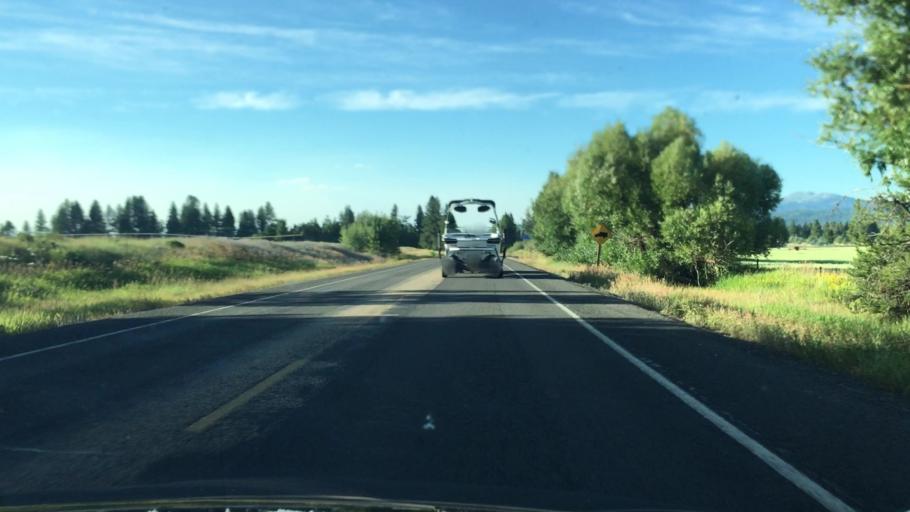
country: US
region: Idaho
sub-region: Valley County
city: Cascade
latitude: 44.6838
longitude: -116.0518
